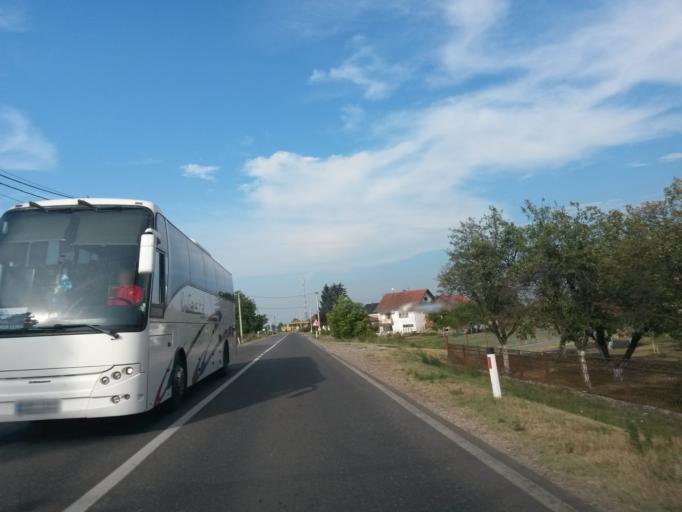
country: BA
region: Republika Srpska
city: Bosanski Samac
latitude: 45.0404
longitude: 18.4493
